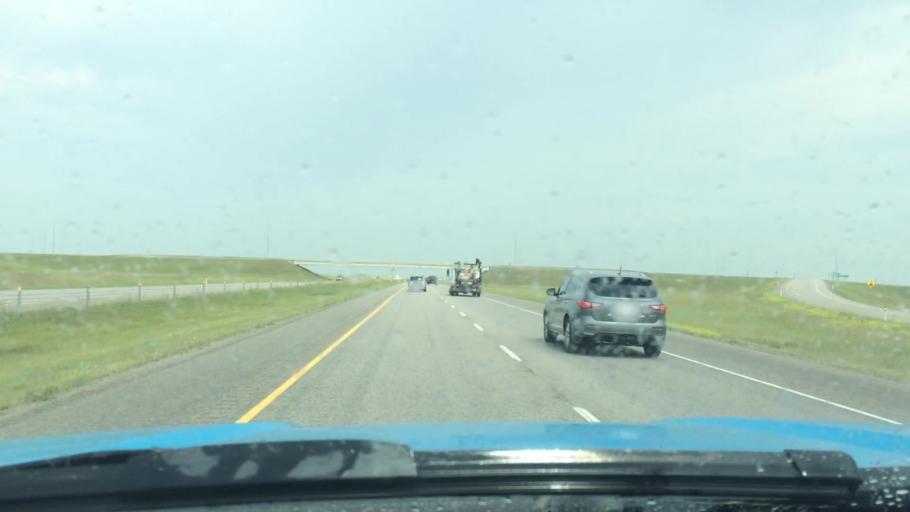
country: CA
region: Alberta
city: Didsbury
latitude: 51.6610
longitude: -114.0254
